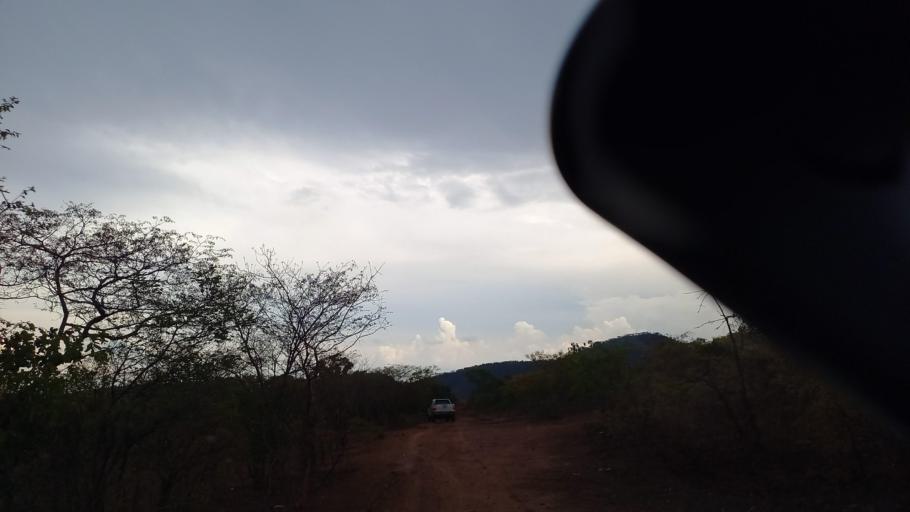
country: ZM
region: Lusaka
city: Kafue
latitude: -16.0272
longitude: 28.2987
